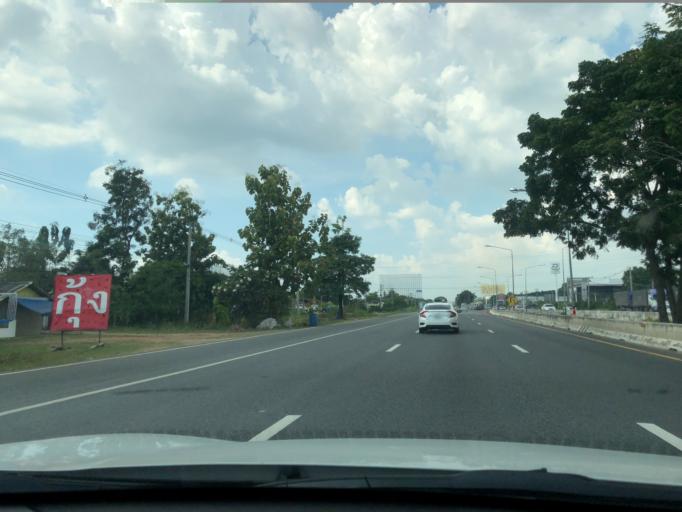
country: TH
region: Nakhon Sawan
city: Krok Phra
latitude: 15.5878
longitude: 100.1238
